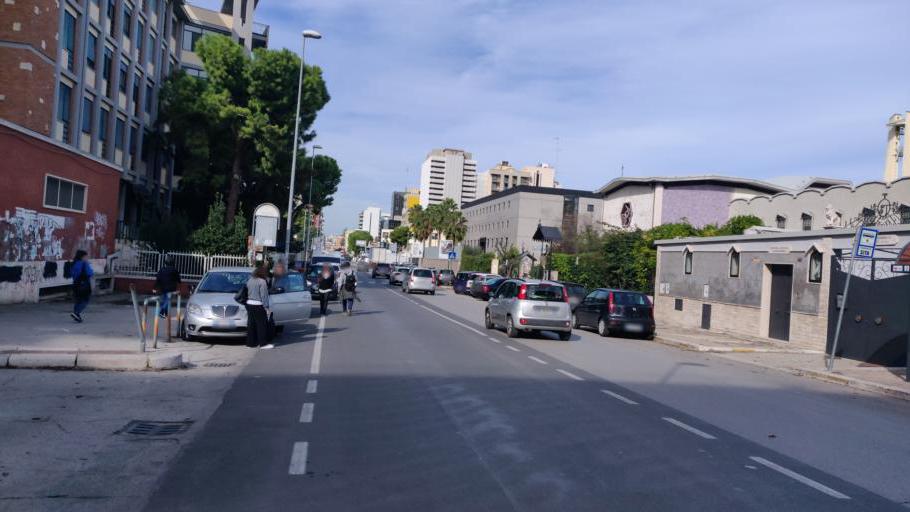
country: IT
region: Apulia
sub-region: Provincia di Bari
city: Bari
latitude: 41.1102
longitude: 16.8837
